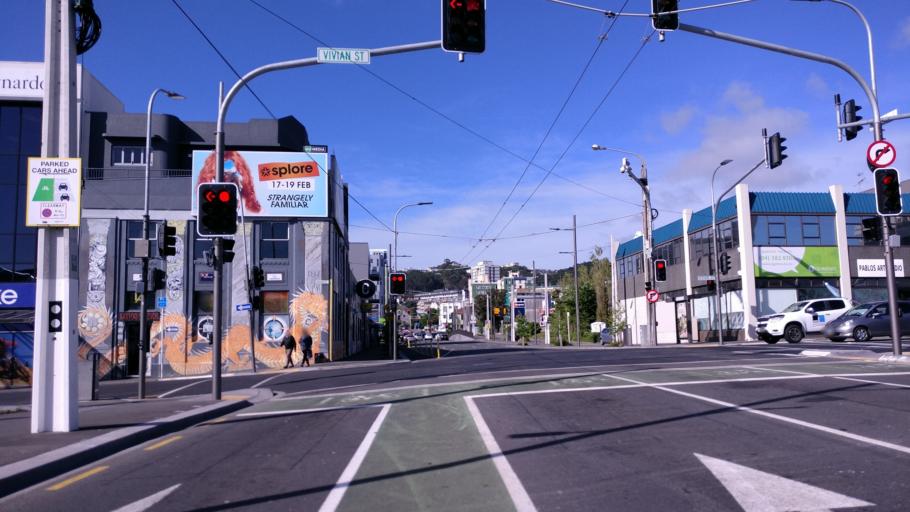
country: NZ
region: Wellington
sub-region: Wellington City
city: Wellington
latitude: -41.2940
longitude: 174.7731
